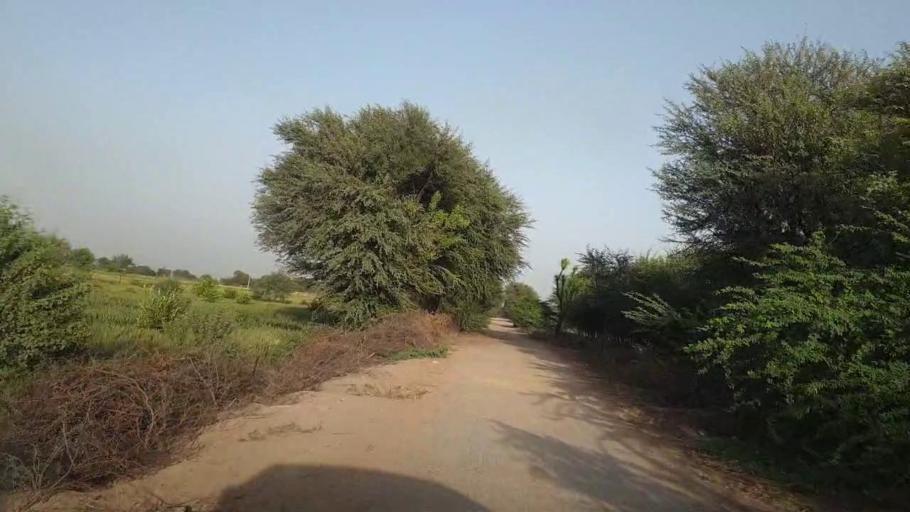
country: PK
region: Sindh
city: Tando Ghulam Ali
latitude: 25.1196
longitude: 68.9180
